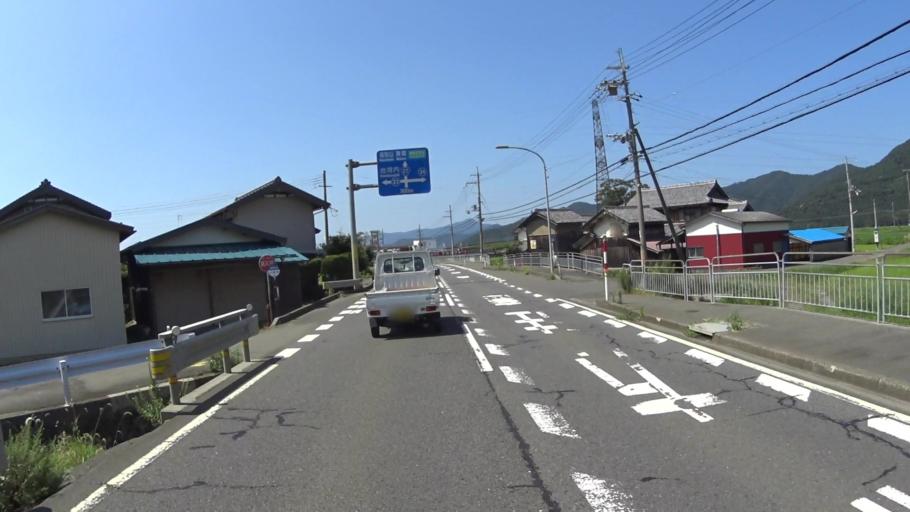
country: JP
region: Fukui
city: Obama
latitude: 35.4760
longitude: 135.7983
